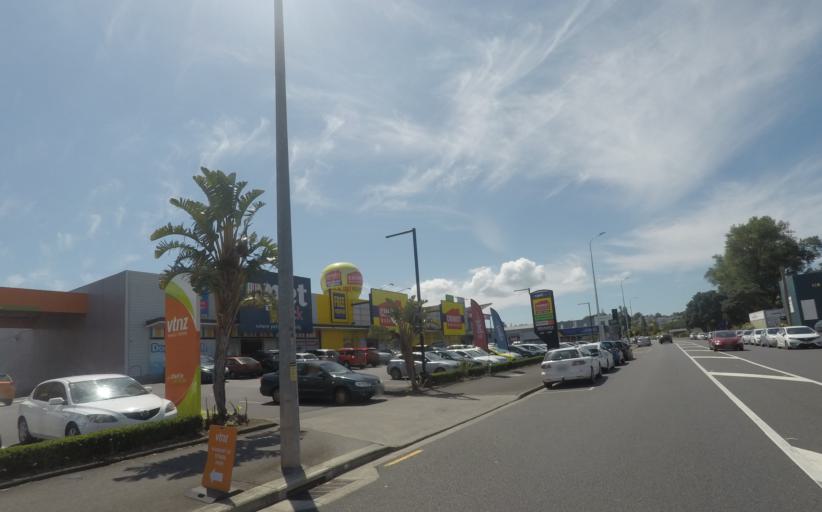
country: NZ
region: Auckland
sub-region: Auckland
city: Tamaki
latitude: -36.8748
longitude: 174.8538
